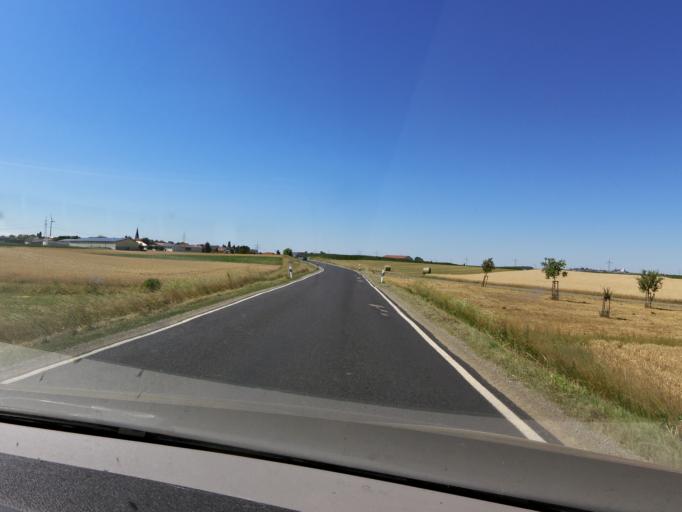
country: DE
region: Bavaria
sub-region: Regierungsbezirk Unterfranken
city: Biebelried
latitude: 49.7403
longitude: 10.0753
